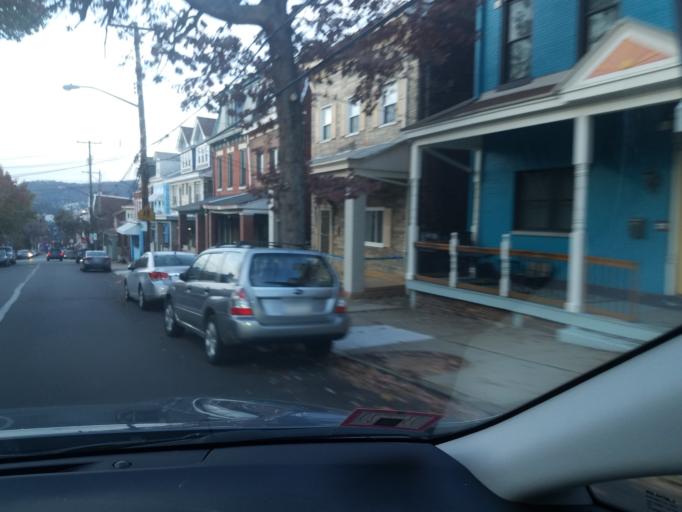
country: US
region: Pennsylvania
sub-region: Allegheny County
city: Bloomfield
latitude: 40.4682
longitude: -79.9586
